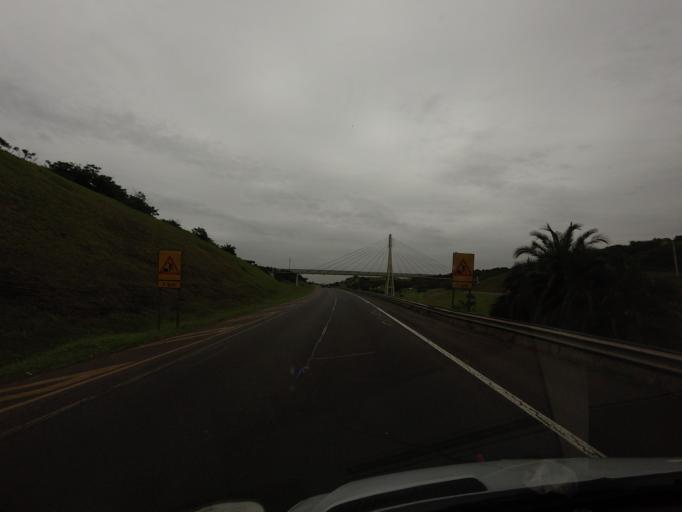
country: ZA
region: KwaZulu-Natal
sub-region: eThekwini Metropolitan Municipality
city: Durban
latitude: -29.6999
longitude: 31.0713
